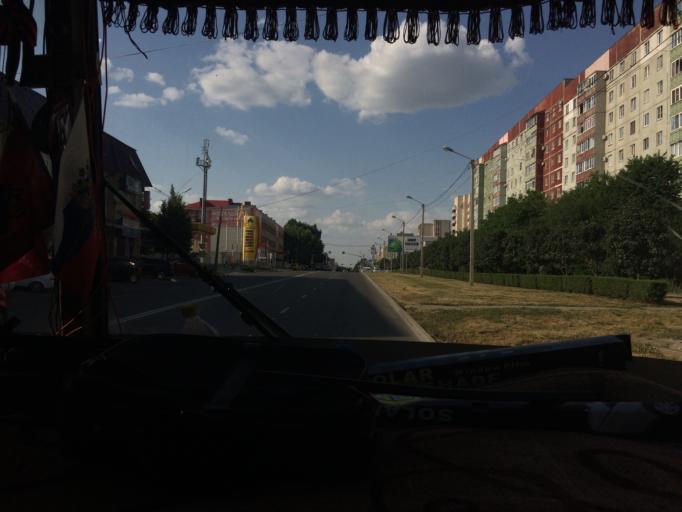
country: RU
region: Stavropol'skiy
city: Tatarka
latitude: 45.0051
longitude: 41.9121
